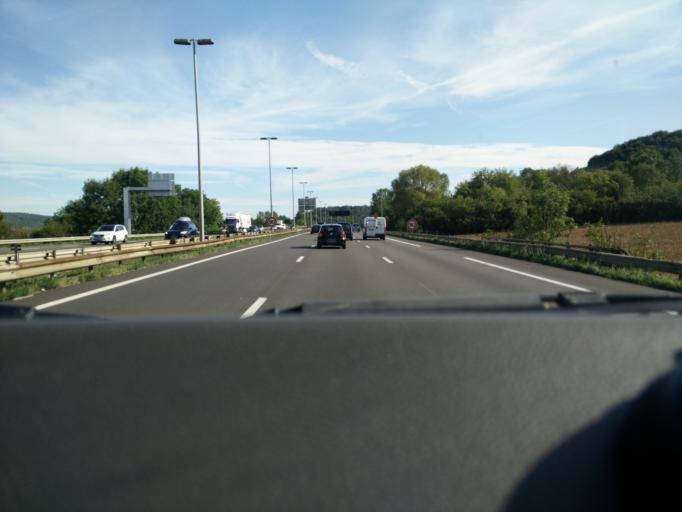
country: FR
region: Lorraine
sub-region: Departement de Meurthe-et-Moselle
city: Champigneulles
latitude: 48.7390
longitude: 6.1547
